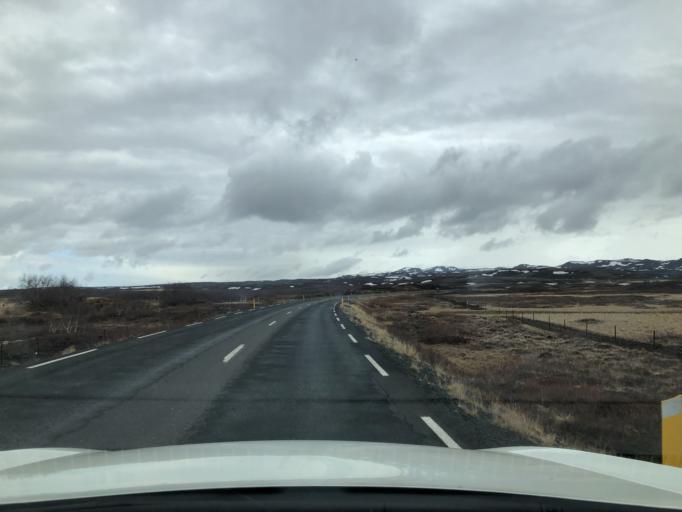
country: IS
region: Northeast
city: Laugar
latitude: 65.6444
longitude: -17.0005
